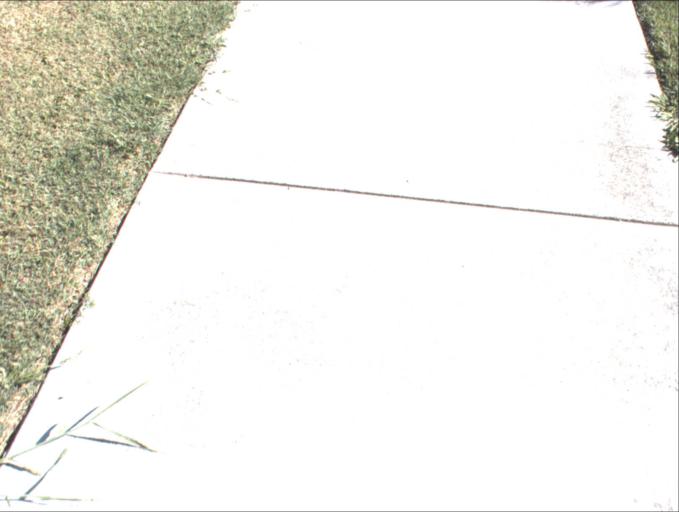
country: AU
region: Queensland
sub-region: Logan
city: Beenleigh
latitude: -27.6910
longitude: 153.2113
